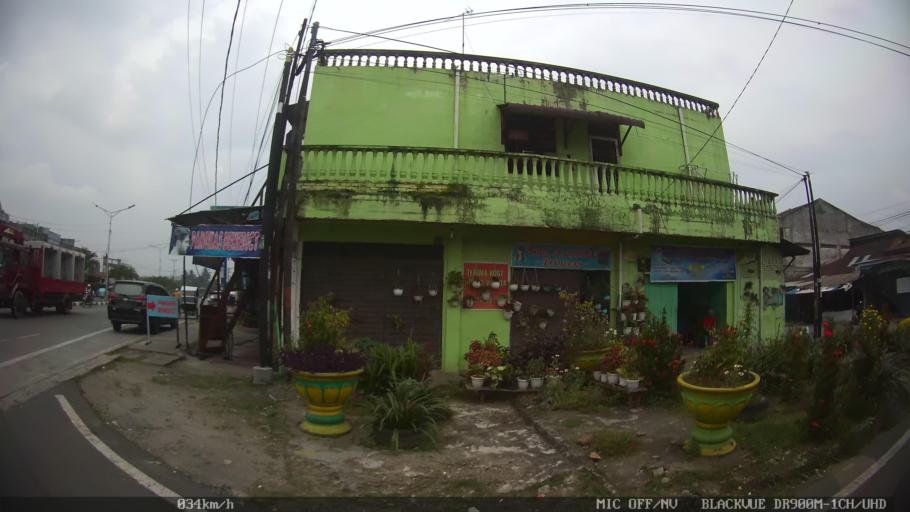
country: ID
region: North Sumatra
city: Deli Tua
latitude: 3.5415
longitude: 98.6989
